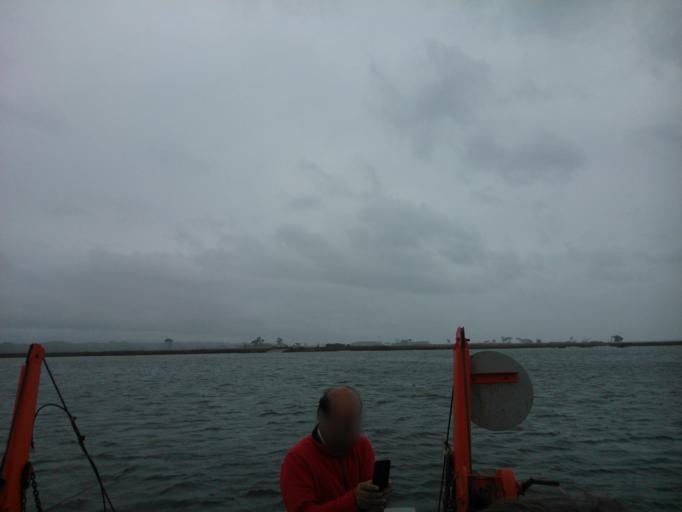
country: CL
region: Araucania
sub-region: Provincia de Cautin
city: Carahue
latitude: -38.7475
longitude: -73.4084
